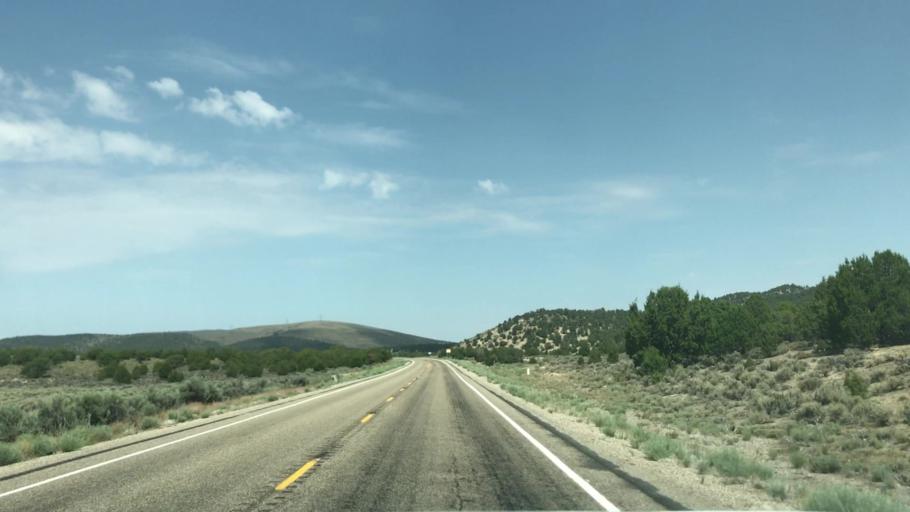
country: US
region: Nevada
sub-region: White Pine County
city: Ely
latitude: 39.3784
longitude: -115.0641
